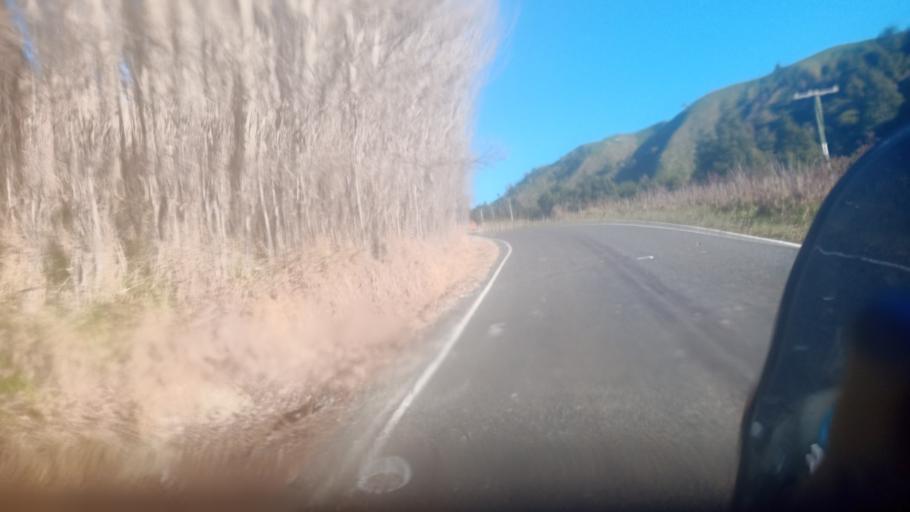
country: NZ
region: Gisborne
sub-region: Gisborne District
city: Gisborne
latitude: -38.5635
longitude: 177.6112
